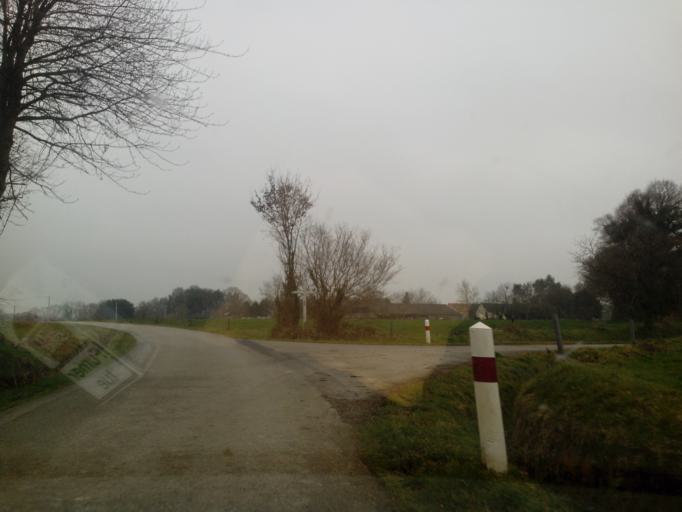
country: FR
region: Brittany
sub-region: Departement du Morbihan
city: Guilliers
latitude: 48.1120
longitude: -2.3838
